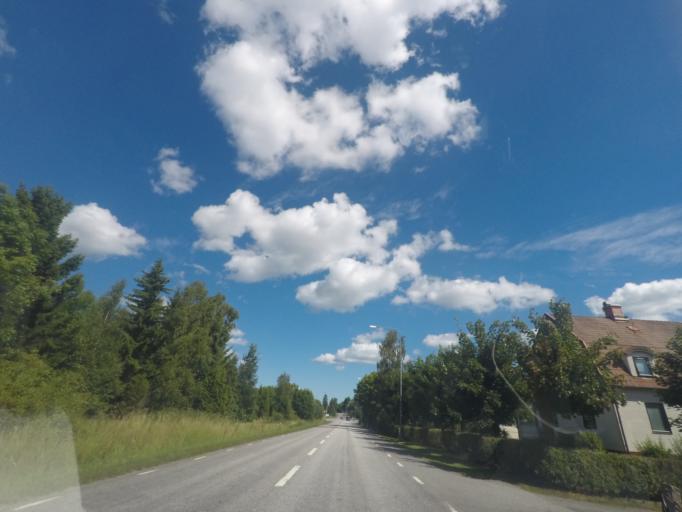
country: SE
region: Stockholm
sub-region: Norrtalje Kommun
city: Hallstavik
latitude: 59.9594
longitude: 18.7956
